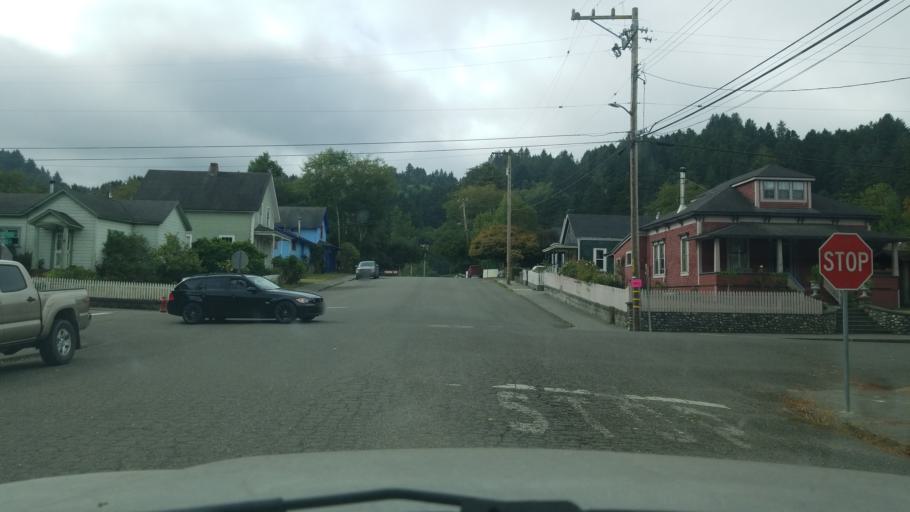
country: US
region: California
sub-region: Humboldt County
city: Ferndale
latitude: 40.5747
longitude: -124.2643
